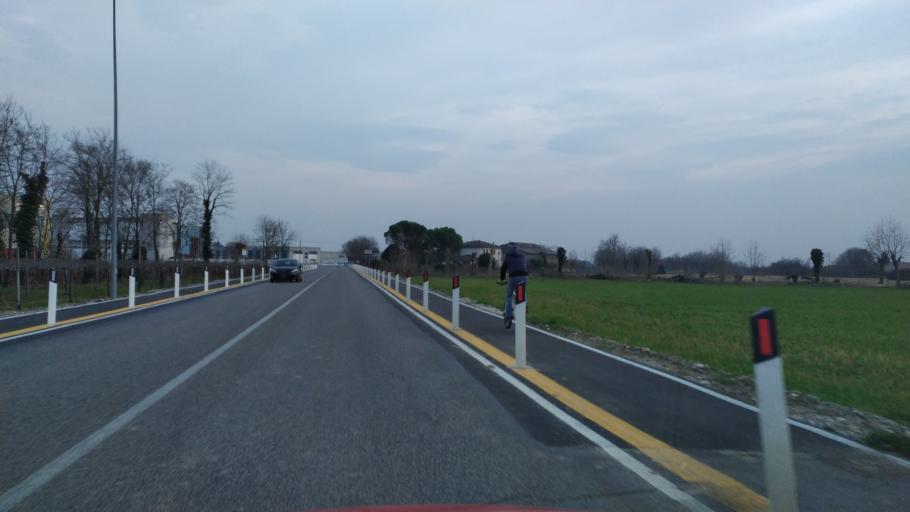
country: IT
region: Veneto
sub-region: Provincia di Vicenza
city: Dueville
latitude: 45.6273
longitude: 11.5639
